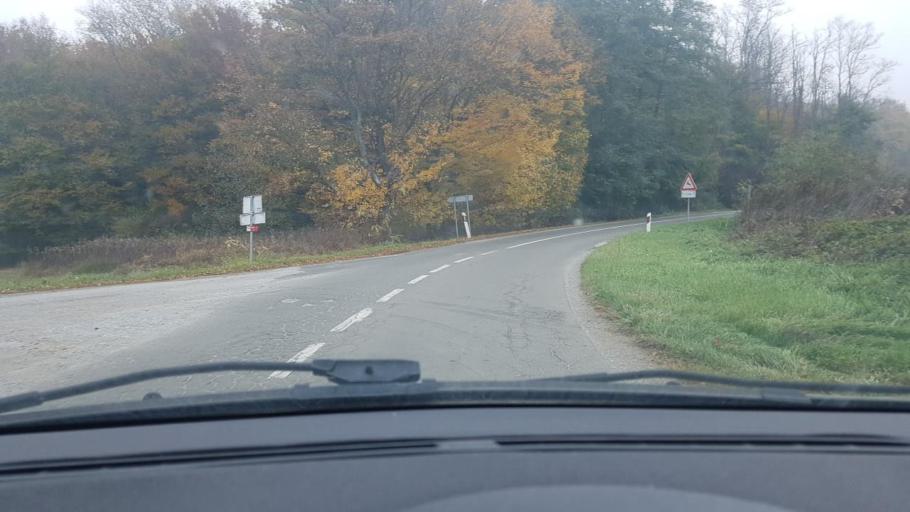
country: HR
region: Varazdinska
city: Ivanec
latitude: 46.1378
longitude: 16.1748
